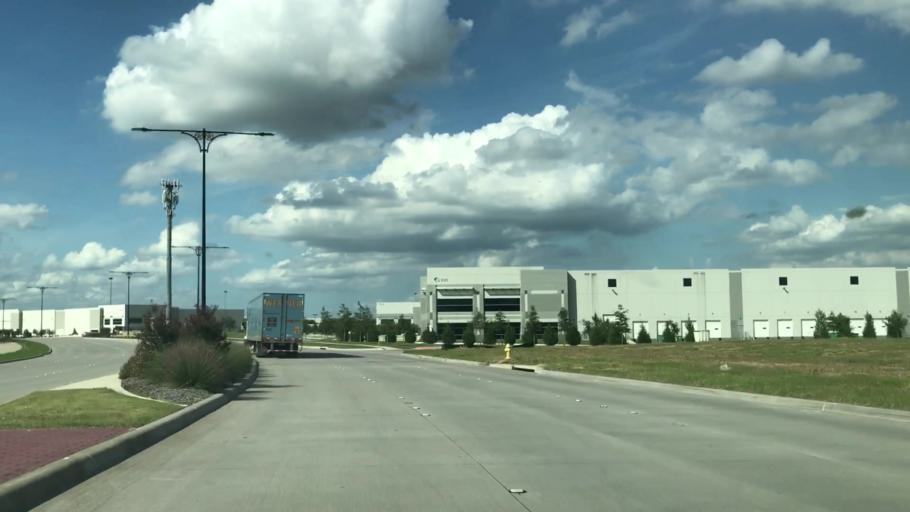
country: US
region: Texas
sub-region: Dallas County
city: Coppell
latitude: 32.9751
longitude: -97.0150
